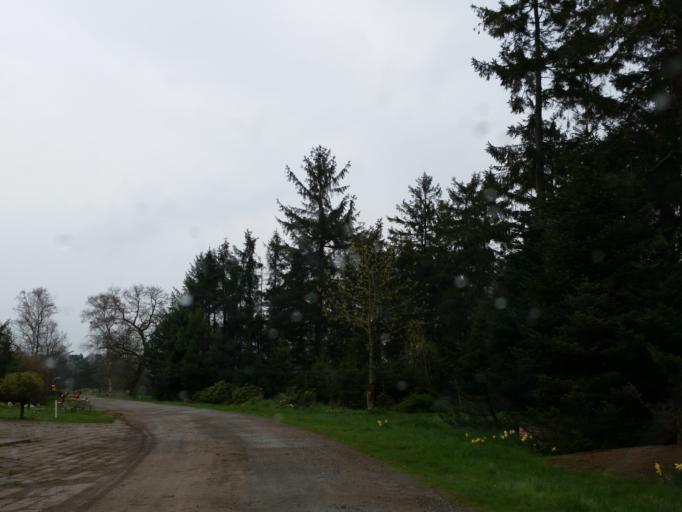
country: DE
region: Lower Saxony
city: Armstorf
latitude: 53.5831
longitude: 9.0106
